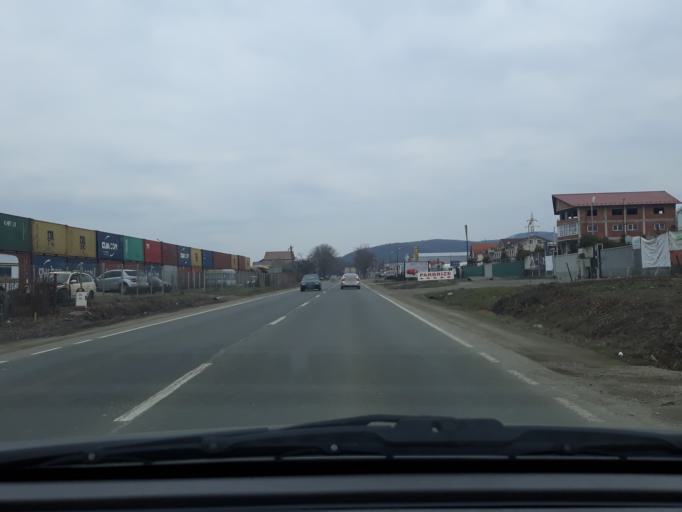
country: RO
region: Salaj
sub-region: Comuna Criseni
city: Criseni
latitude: 47.2237
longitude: 23.0306
